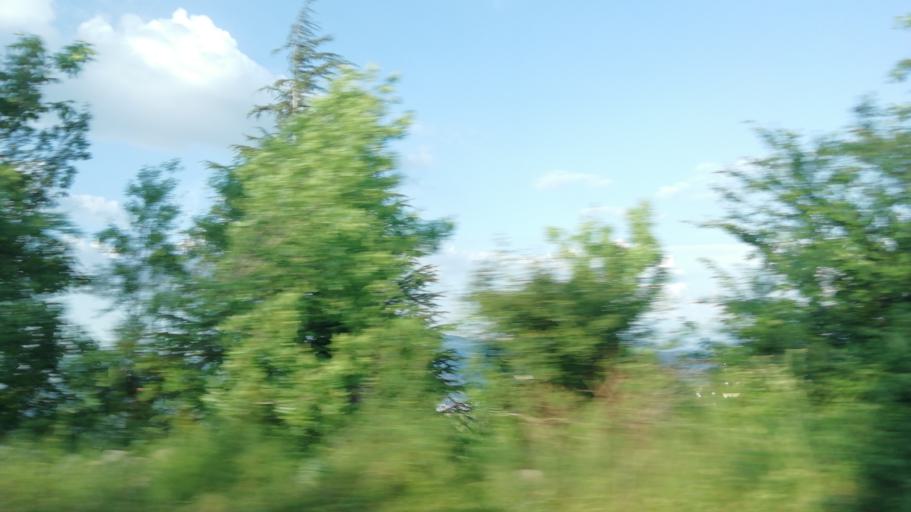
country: TR
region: Karabuk
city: Karabuk
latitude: 41.1271
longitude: 32.6131
